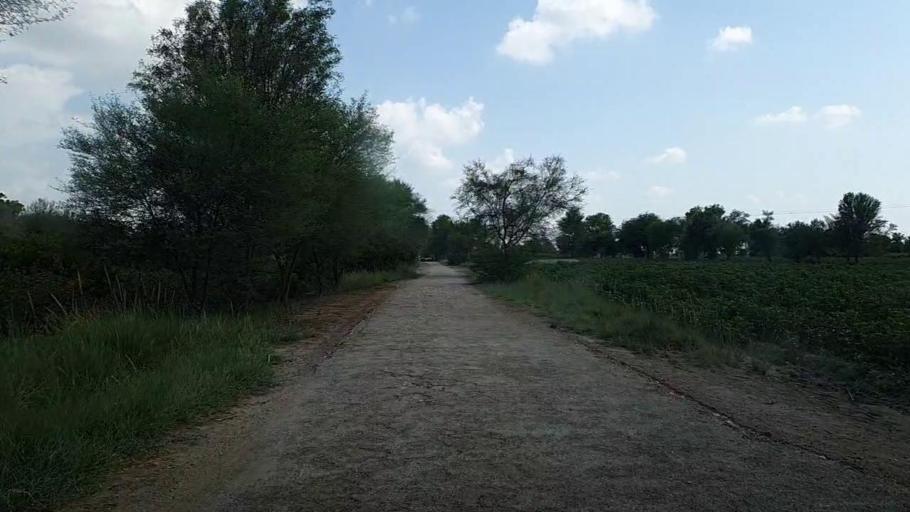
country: PK
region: Sindh
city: Kandiaro
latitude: 26.9927
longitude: 68.3053
